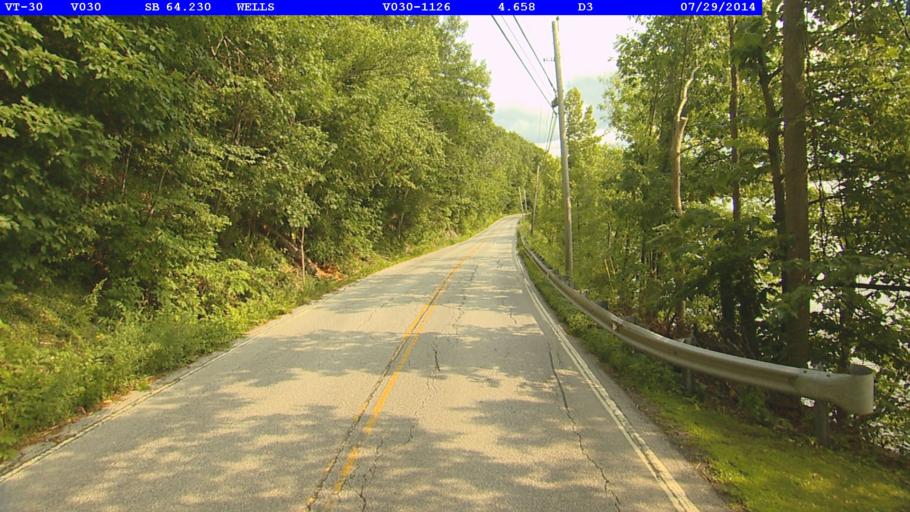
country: US
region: Vermont
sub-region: Rutland County
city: Poultney
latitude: 43.4579
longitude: -73.2055
